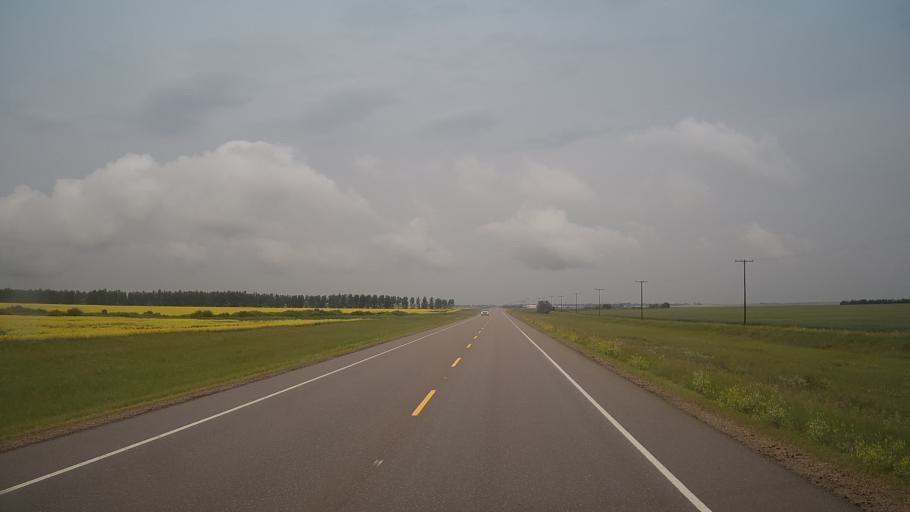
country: CA
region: Saskatchewan
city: Wilkie
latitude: 52.3410
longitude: -108.7138
